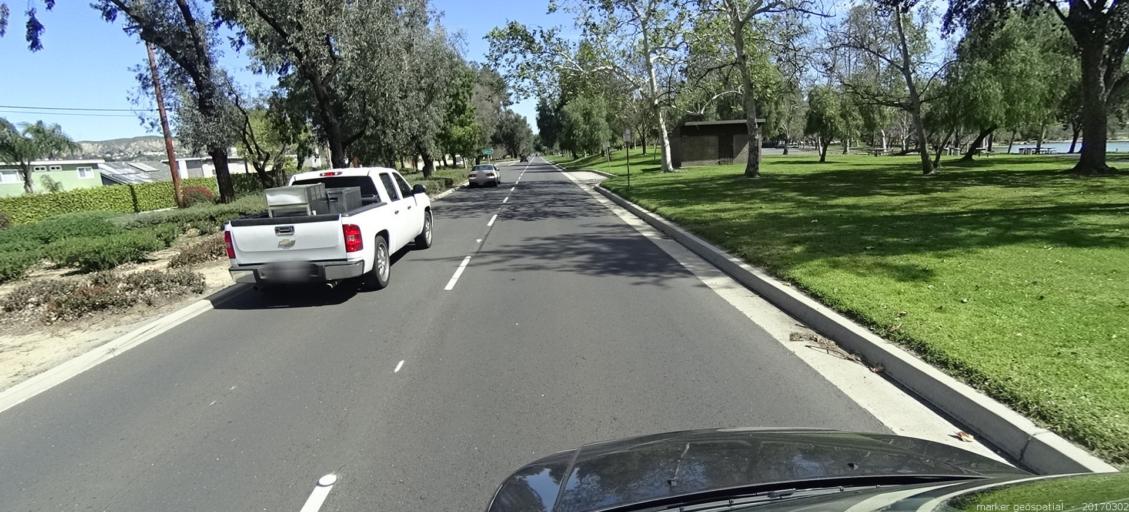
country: US
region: California
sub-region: Orange County
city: Yorba Linda
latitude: 33.8707
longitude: -117.7668
